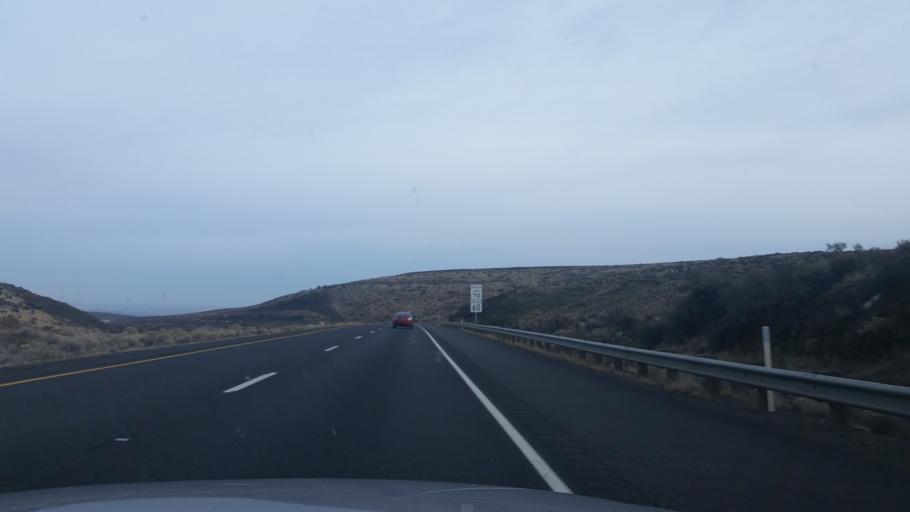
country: US
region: Washington
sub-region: Kittitas County
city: Kittitas
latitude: 46.9439
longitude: -120.1863
